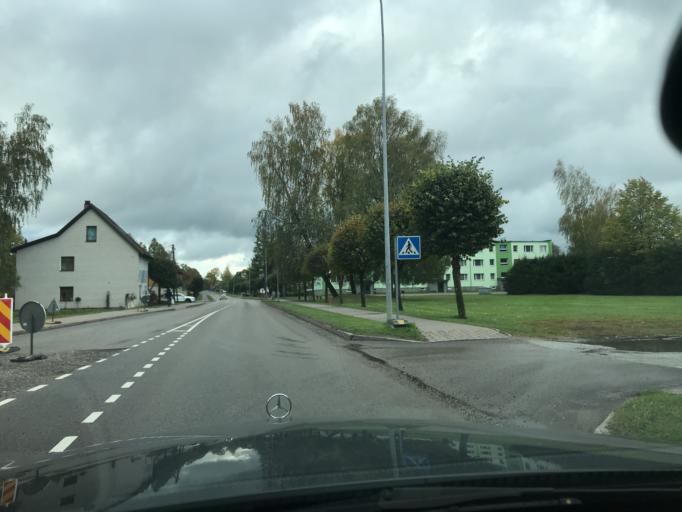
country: EE
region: Valgamaa
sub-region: Torva linn
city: Torva
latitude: 58.0023
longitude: 25.9238
